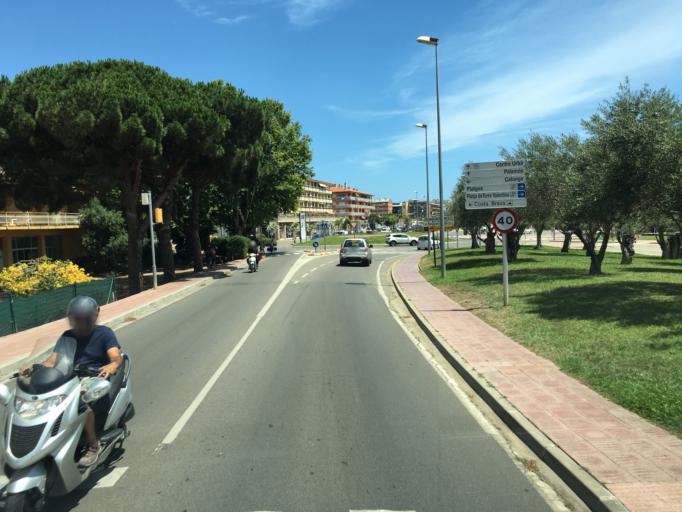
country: ES
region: Catalonia
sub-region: Provincia de Girona
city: Calonge
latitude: 41.8448
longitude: 3.0947
